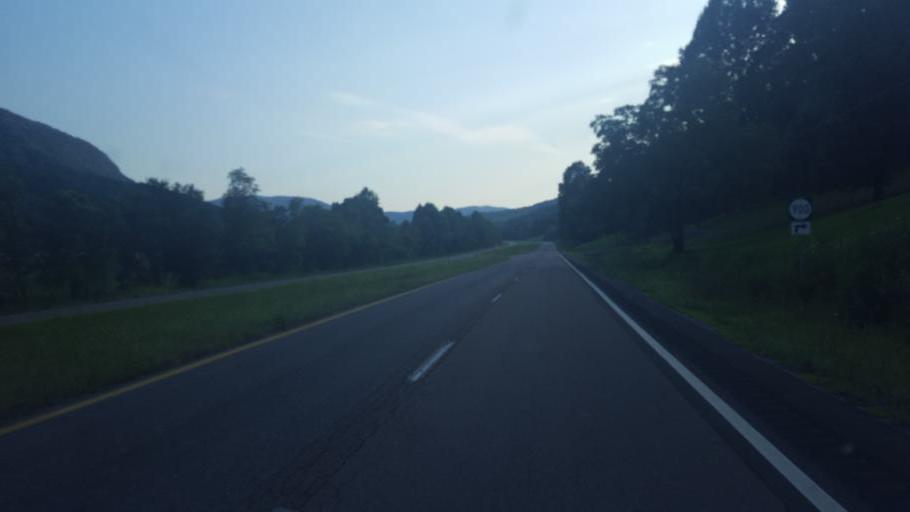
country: US
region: Virginia
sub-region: Wise County
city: Big Stone Gap
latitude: 36.7962
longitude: -82.8049
